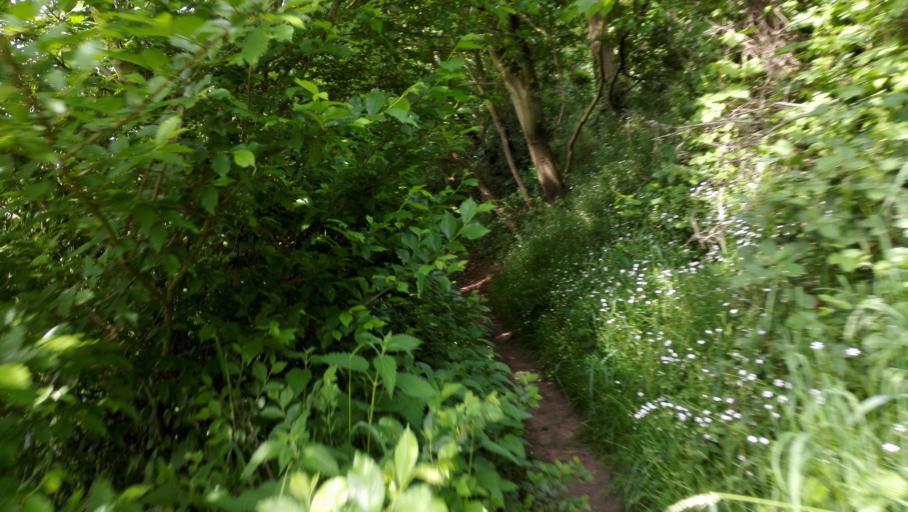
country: BE
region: Flanders
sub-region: Provincie Vlaams-Brabant
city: Holsbeek
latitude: 50.8767
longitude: 4.7575
